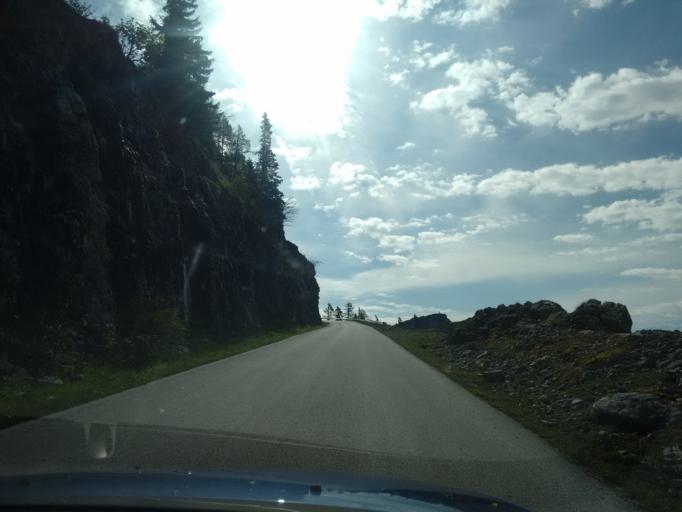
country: AT
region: Styria
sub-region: Politischer Bezirk Liezen
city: Altaussee
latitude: 47.6560
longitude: 13.7808
